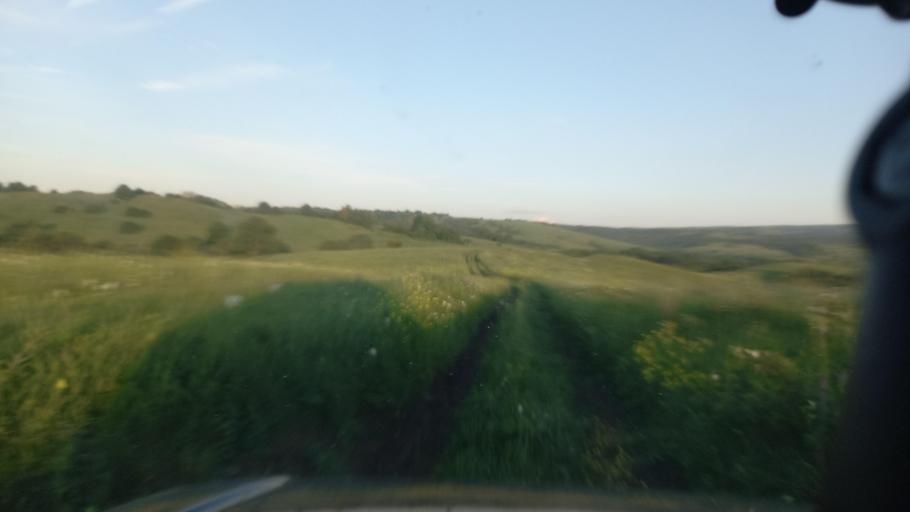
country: RU
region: Karachayevo-Cherkesiya
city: Pregradnaya
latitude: 44.1193
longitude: 41.1161
